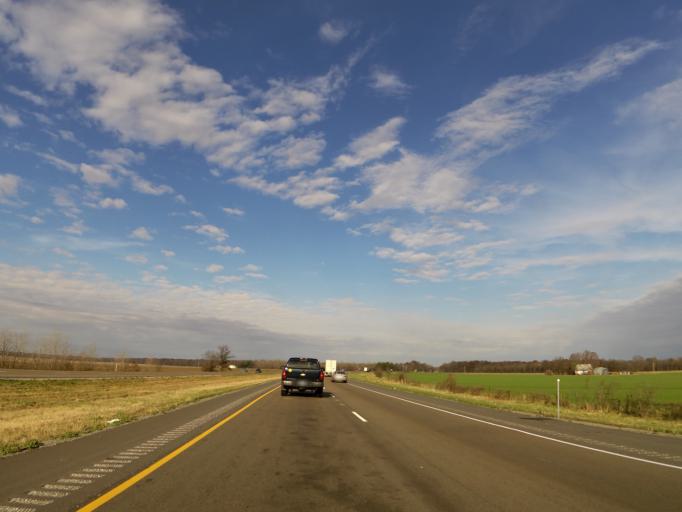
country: US
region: Illinois
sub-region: Washington County
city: Okawville
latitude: 38.4582
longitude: -89.5645
